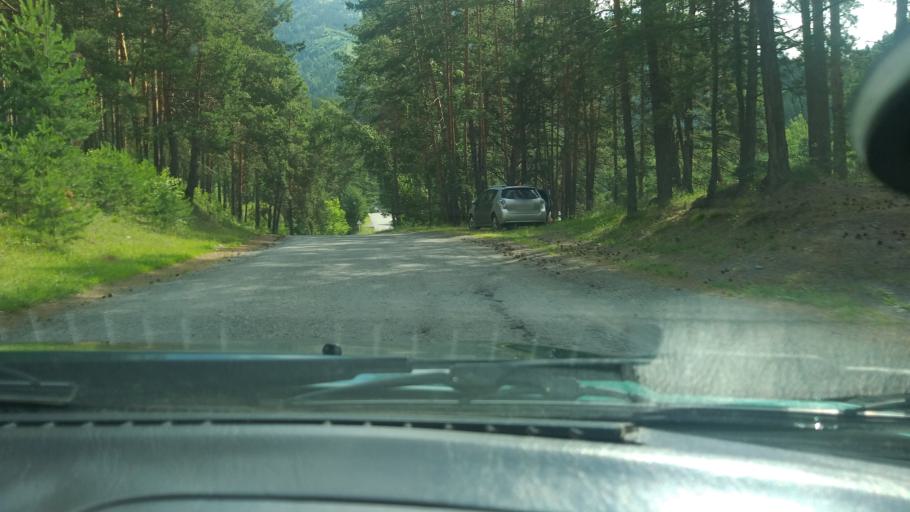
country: RU
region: Altay
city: Chemal
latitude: 51.3911
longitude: 86.0375
